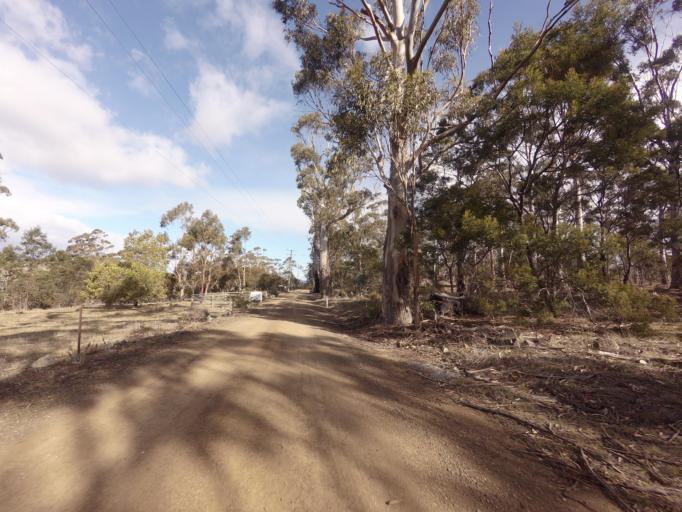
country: AU
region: Tasmania
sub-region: Sorell
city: Sorell
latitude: -42.3299
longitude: 147.9676
